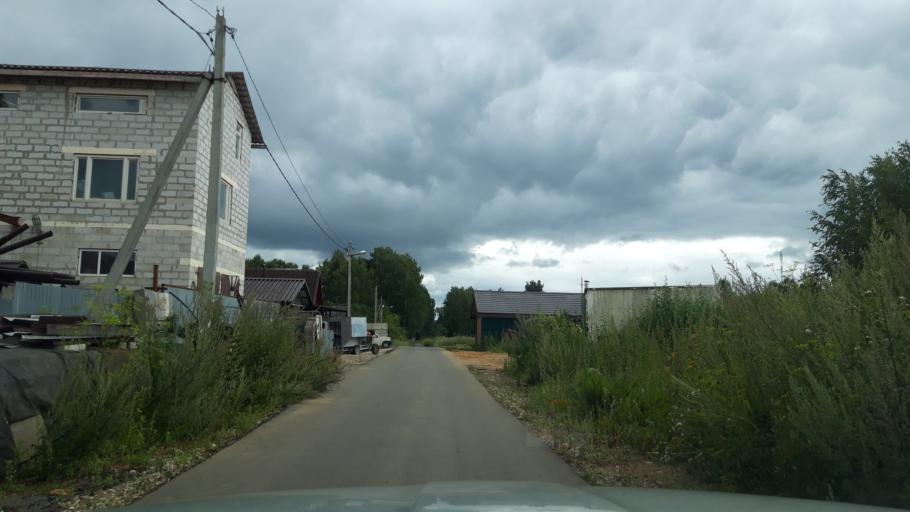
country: RU
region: Moskovskaya
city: Povarovo
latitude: 56.0720
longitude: 37.0689
